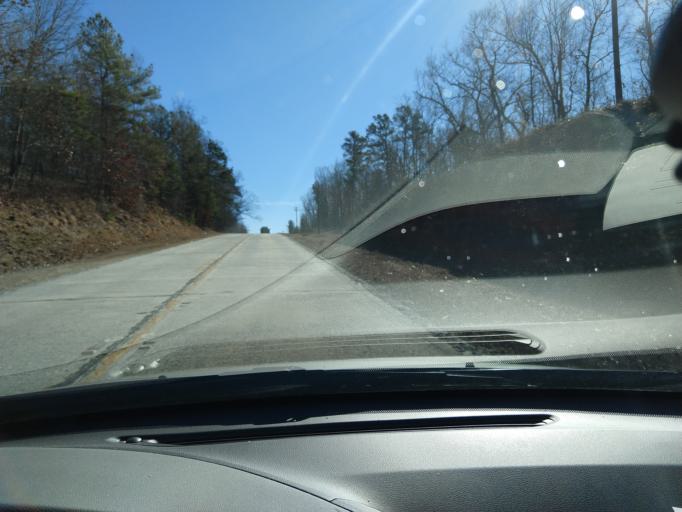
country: US
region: Georgia
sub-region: Habersham County
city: Clarkesville
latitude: 34.6189
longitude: -83.4303
